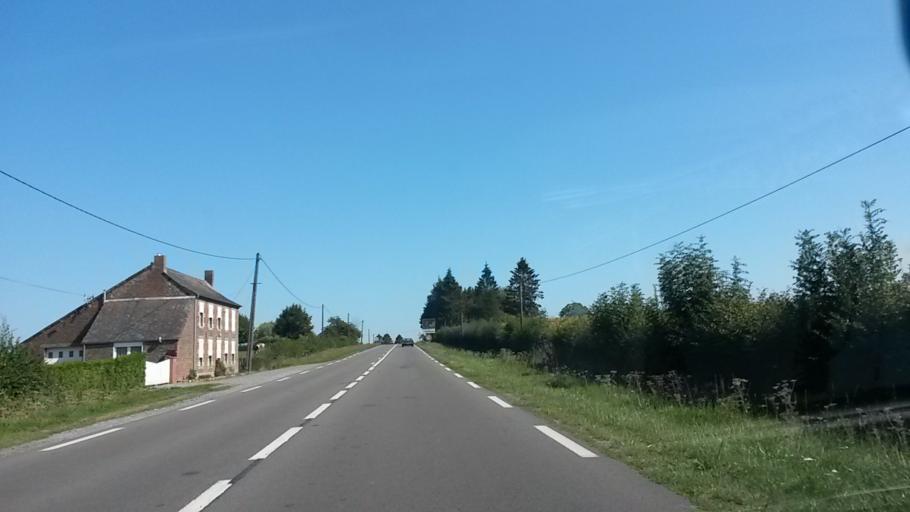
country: FR
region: Nord-Pas-de-Calais
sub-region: Departement du Nord
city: Avesnelles
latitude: 50.1507
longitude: 3.9522
